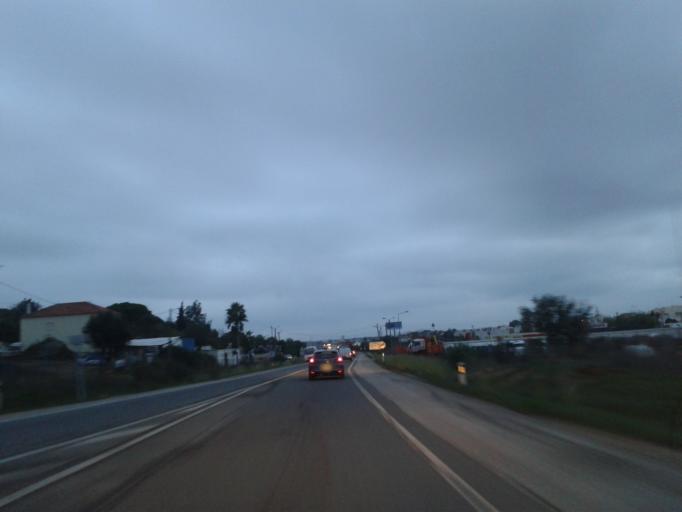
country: PT
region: Faro
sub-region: Albufeira
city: Ferreiras
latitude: 37.1231
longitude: -8.2253
